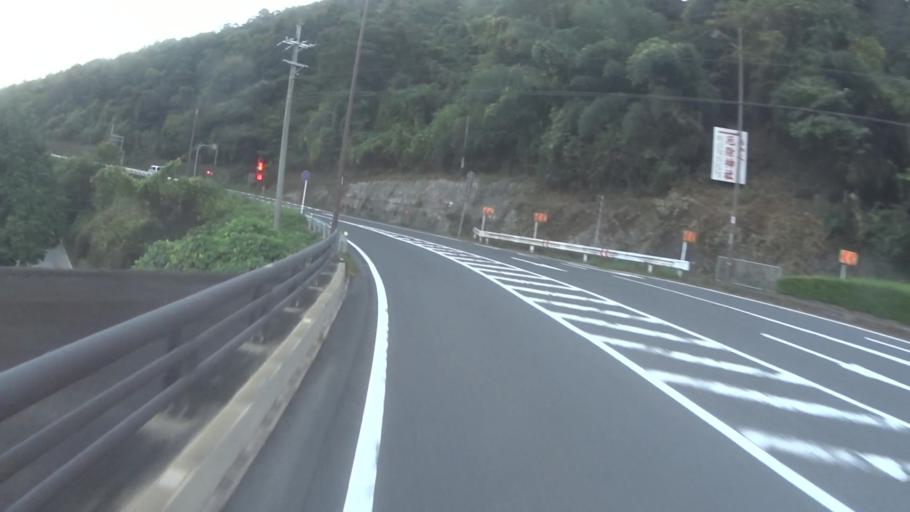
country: JP
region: Kyoto
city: Ayabe
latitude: 35.2889
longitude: 135.2652
